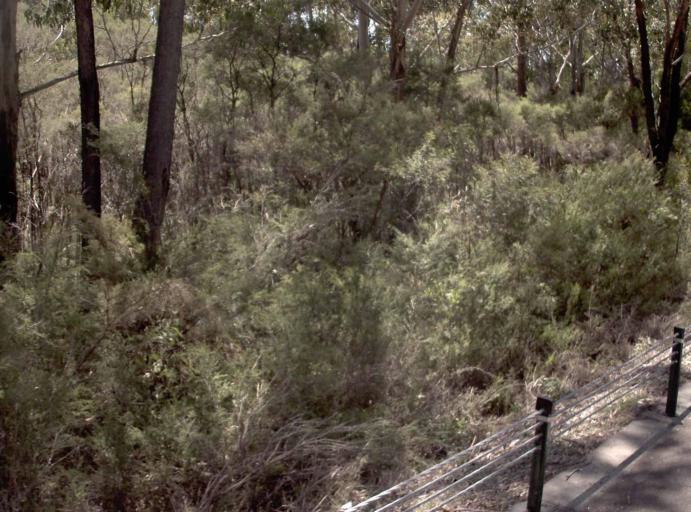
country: AU
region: Victoria
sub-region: East Gippsland
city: Lakes Entrance
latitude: -37.7471
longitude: 148.0719
